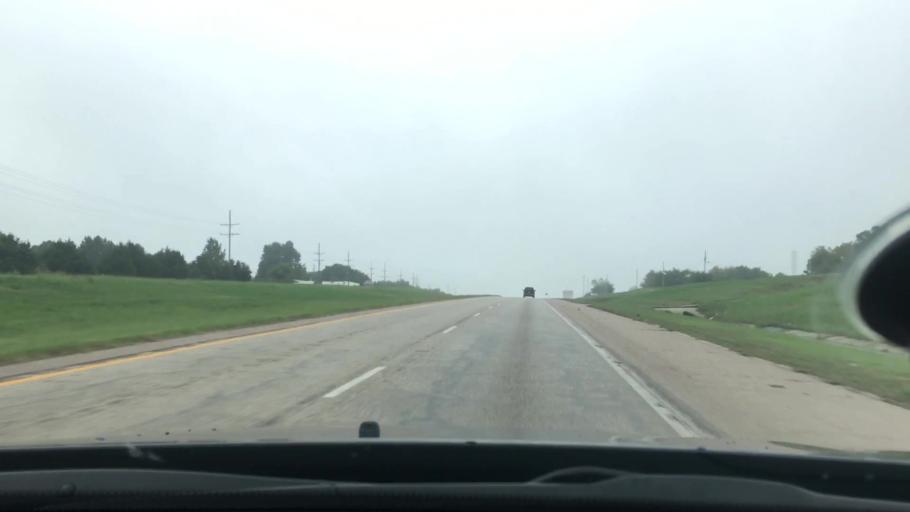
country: US
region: Oklahoma
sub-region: Seminole County
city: Seminole
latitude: 35.2856
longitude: -96.6707
